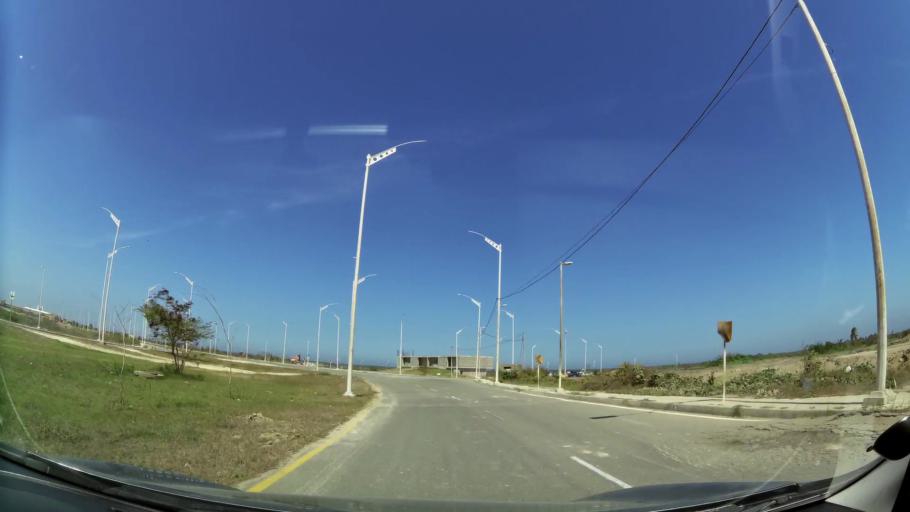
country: CO
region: Atlantico
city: Barranquilla
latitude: 10.9943
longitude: -74.7698
